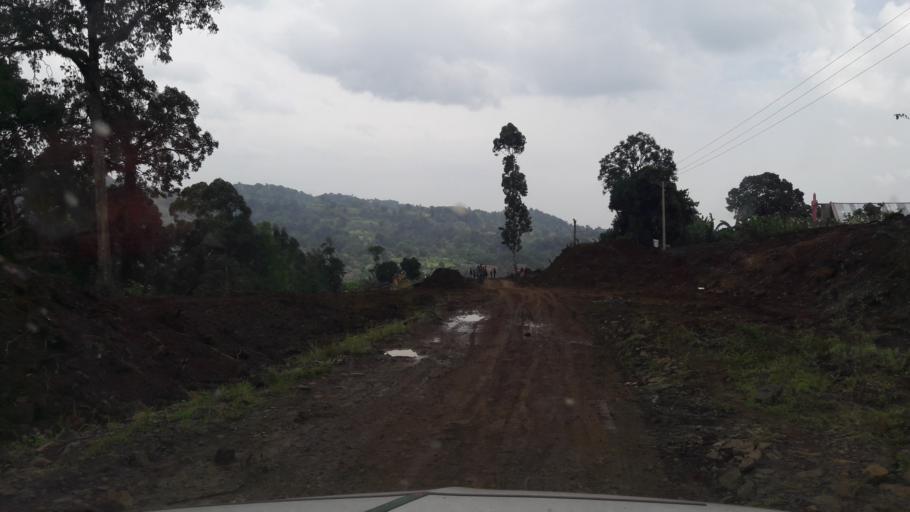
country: ET
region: Southern Nations, Nationalities, and People's Region
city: Tippi
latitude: 7.6488
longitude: 35.5063
